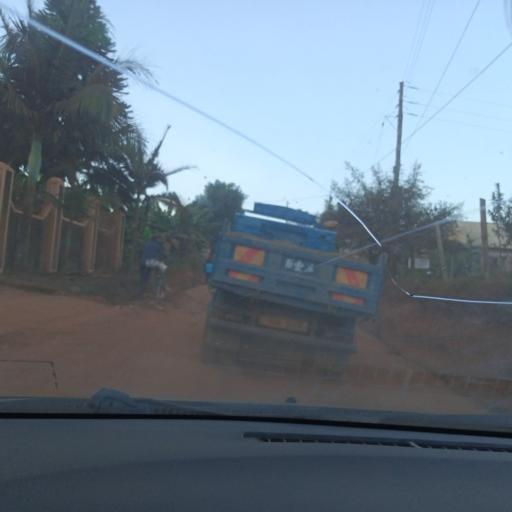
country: UG
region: Central Region
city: Masaka
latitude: -0.3168
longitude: 31.7696
